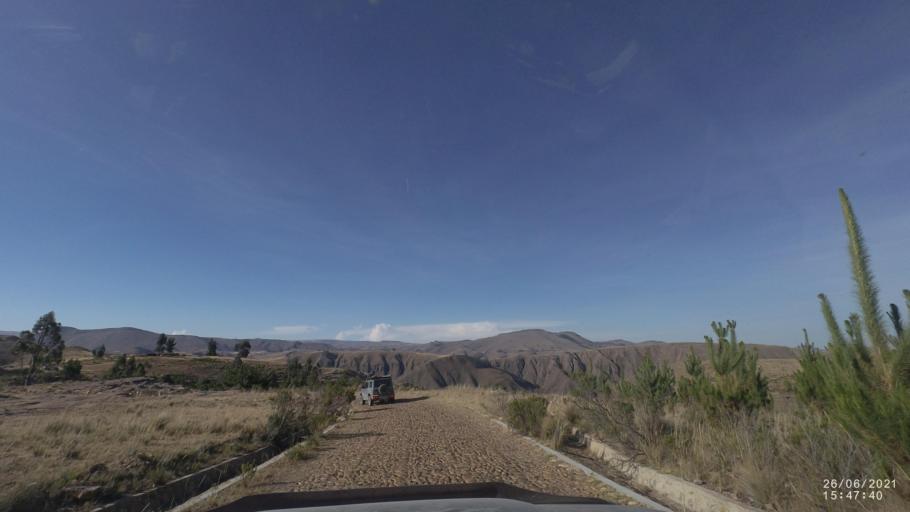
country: BO
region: Cochabamba
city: Arani
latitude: -17.8684
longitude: -65.6982
